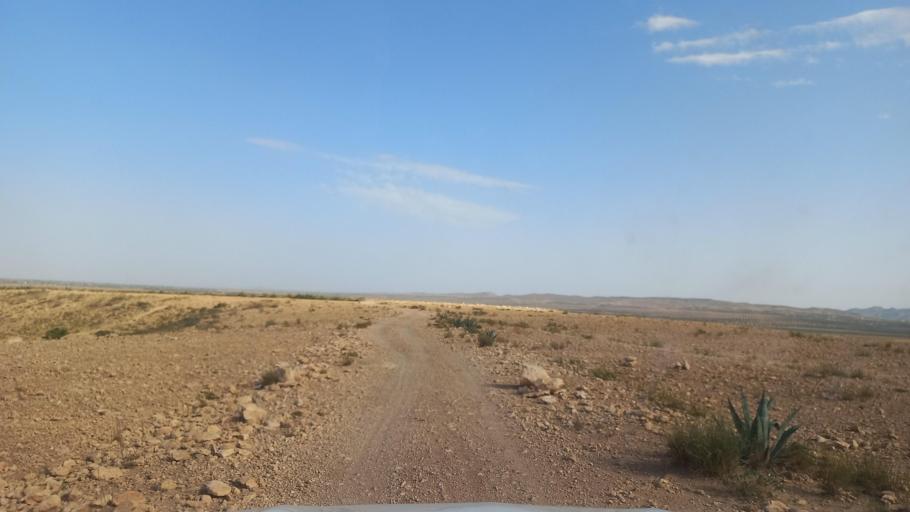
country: TN
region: Al Qasrayn
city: Kasserine
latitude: 35.2591
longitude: 8.9297
